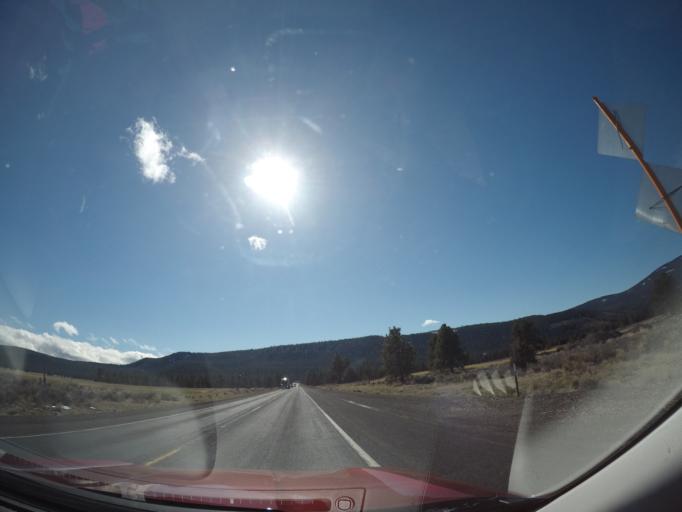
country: US
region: California
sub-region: Siskiyou County
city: Montague
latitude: 41.7655
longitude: -122.0589
